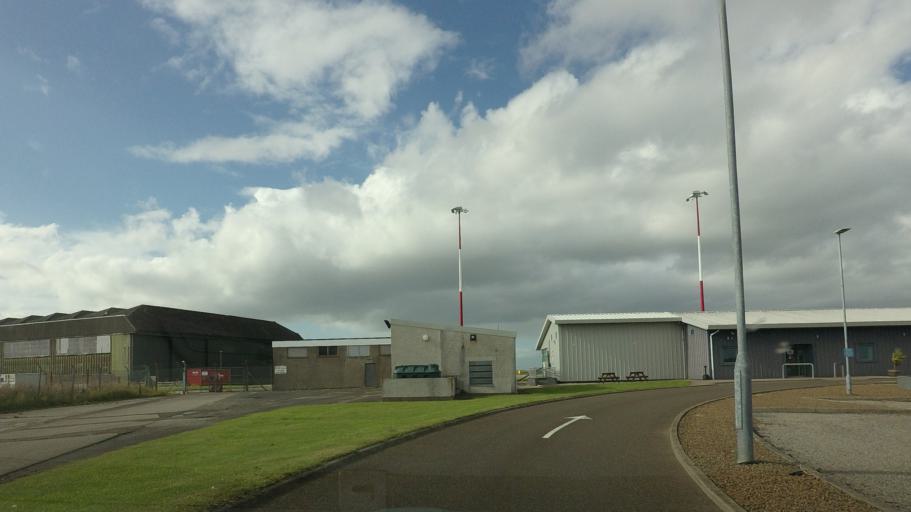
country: GB
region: Scotland
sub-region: Highland
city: Wick
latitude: 58.4533
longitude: -3.0873
